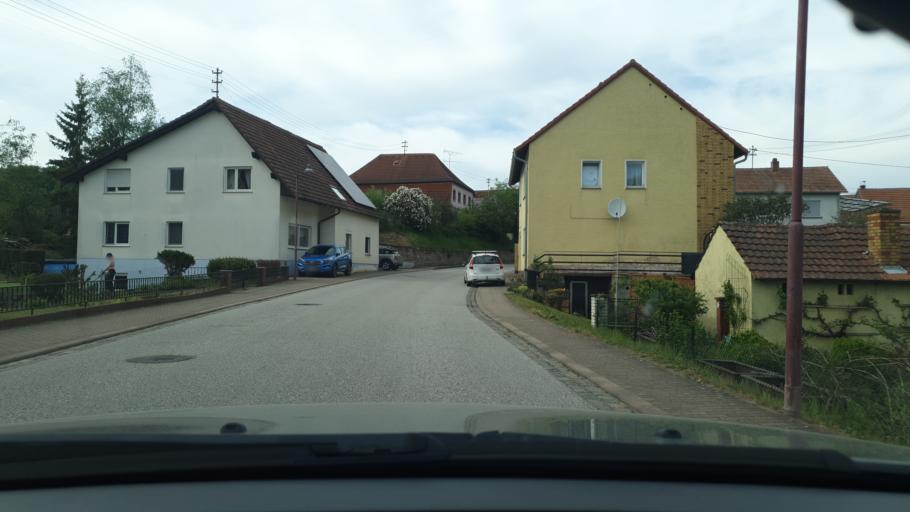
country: DE
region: Rheinland-Pfalz
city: Mittelbrunn
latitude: 49.3697
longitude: 7.5495
